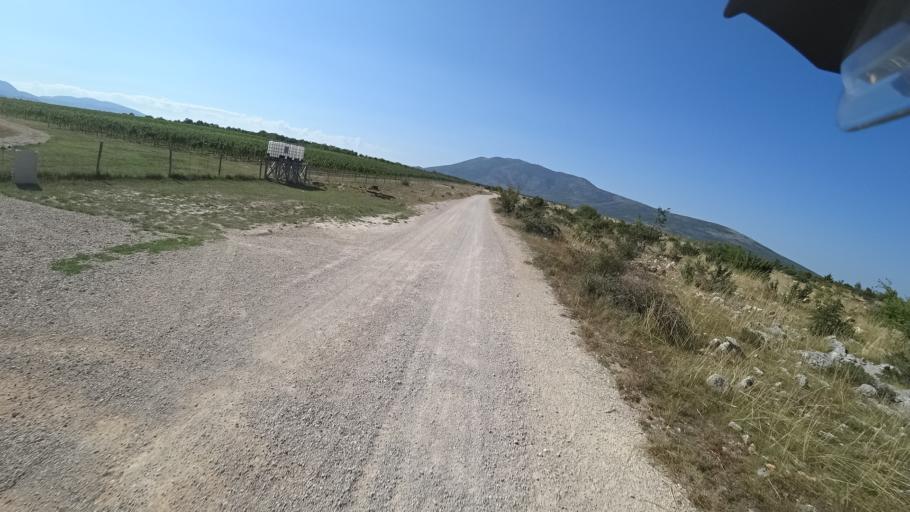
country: HR
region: Sibensko-Kniniska
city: Knin
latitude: 43.9920
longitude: 16.1928
